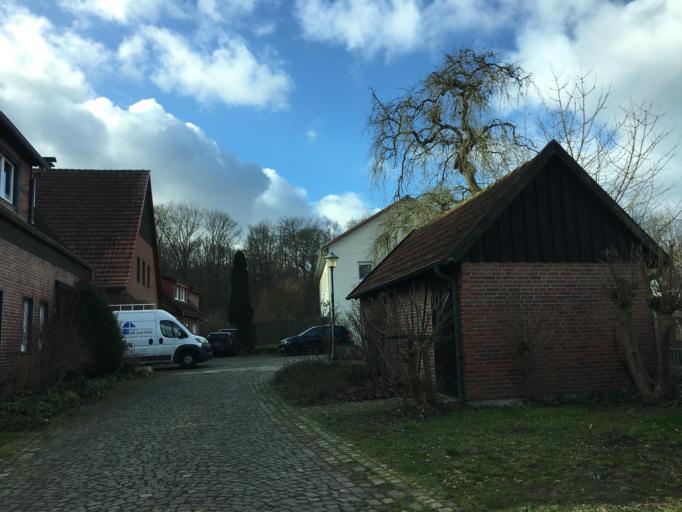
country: DE
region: North Rhine-Westphalia
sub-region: Regierungsbezirk Munster
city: Havixbeck
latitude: 51.9957
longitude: 7.4604
